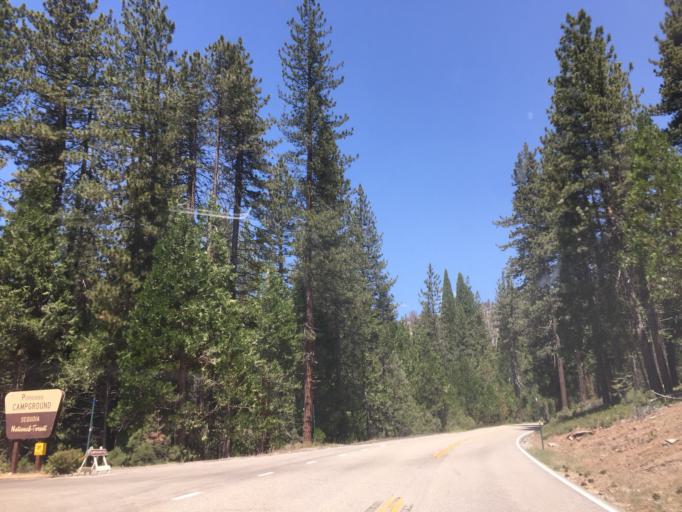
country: US
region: California
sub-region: Fresno County
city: Squaw Valley
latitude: 36.8027
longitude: -118.9375
